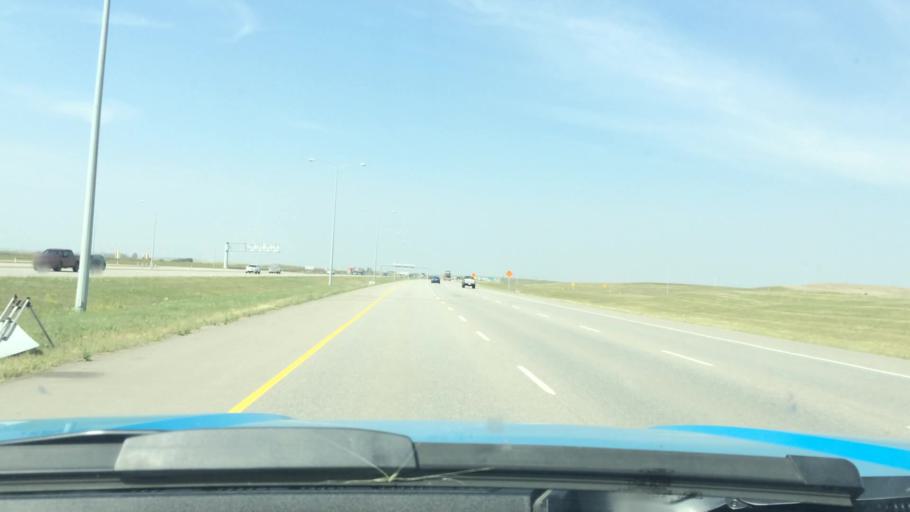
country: CA
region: Alberta
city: Chestermere
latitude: 50.9825
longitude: -113.9205
